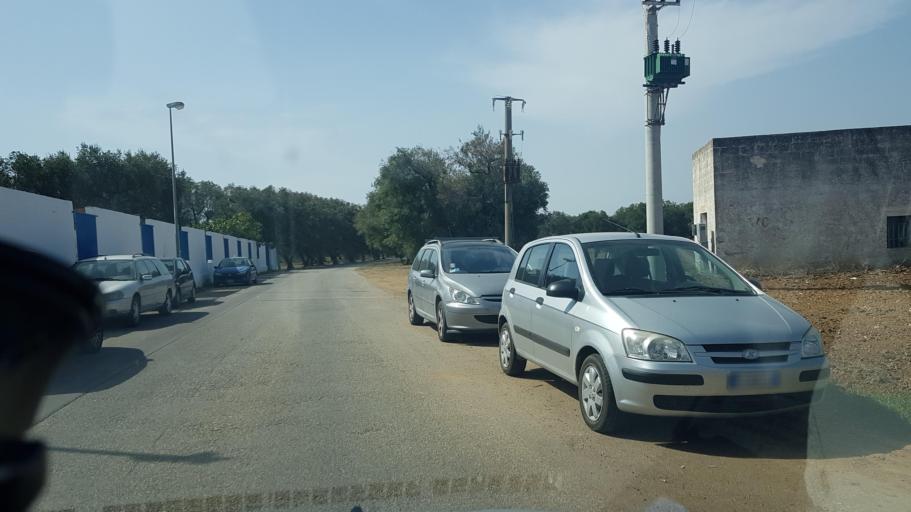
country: IT
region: Apulia
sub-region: Provincia di Brindisi
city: Mesagne
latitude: 40.5703
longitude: 17.8318
